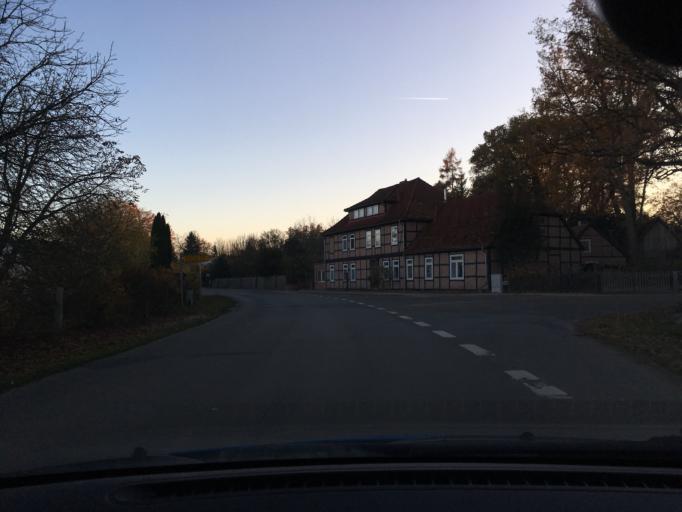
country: DE
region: Lower Saxony
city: Natendorf
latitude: 53.1090
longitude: 10.4550
